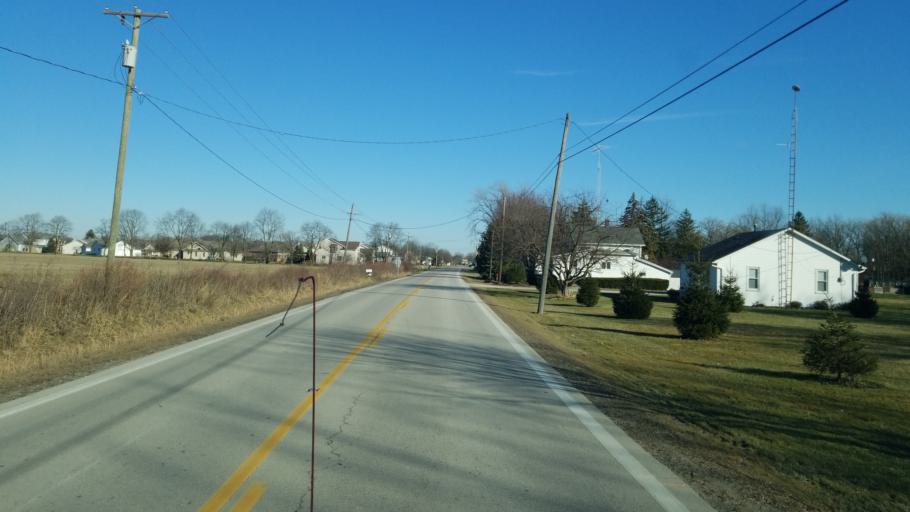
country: US
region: Ohio
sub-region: Sandusky County
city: Woodville
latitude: 41.4501
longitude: -83.3814
